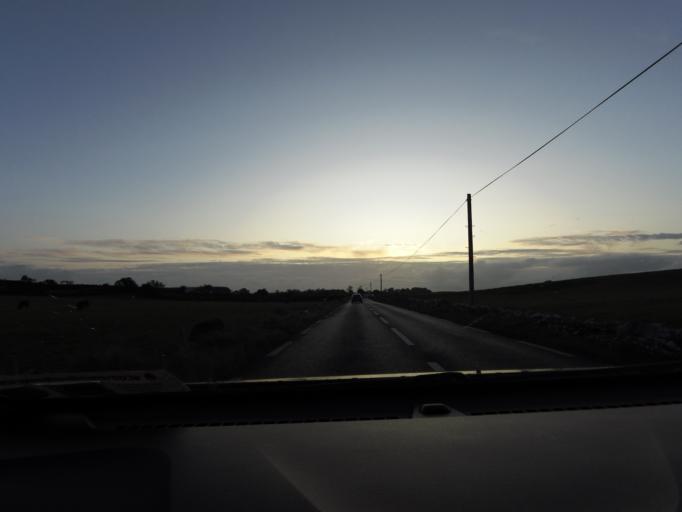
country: IE
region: Connaught
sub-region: County Galway
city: Athenry
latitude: 53.4818
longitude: -8.5976
